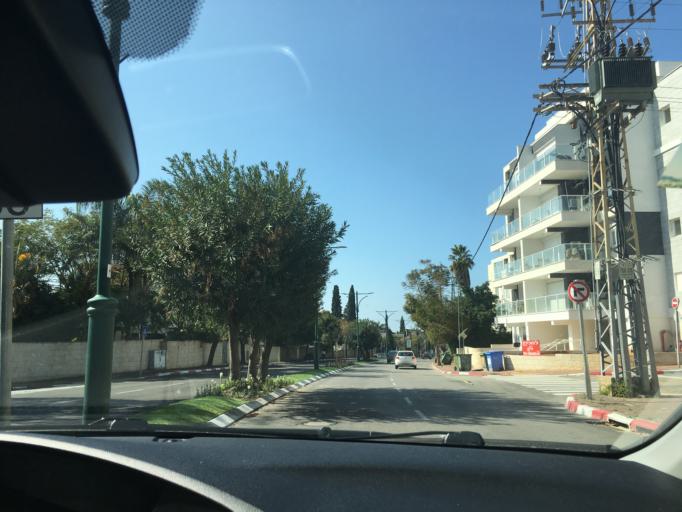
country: IL
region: Tel Aviv
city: Ramat HaSharon
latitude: 32.1597
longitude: 34.8470
